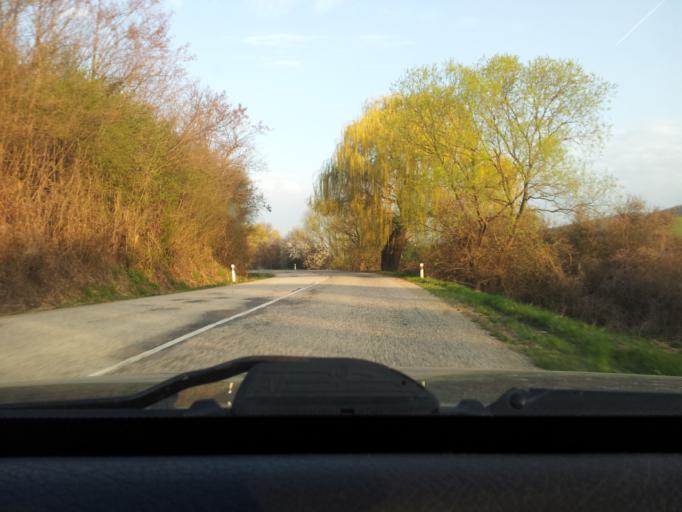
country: SK
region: Nitriansky
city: Tlmace
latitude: 48.2805
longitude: 18.4801
